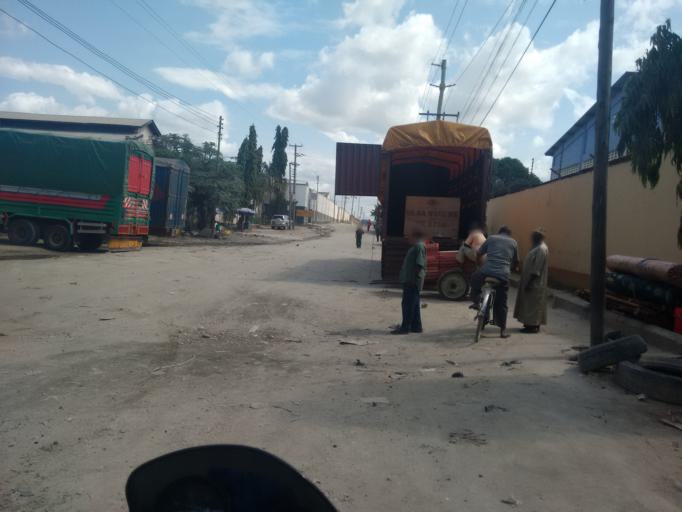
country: TZ
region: Dar es Salaam
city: Dar es Salaam
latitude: -6.8419
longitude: 39.2659
